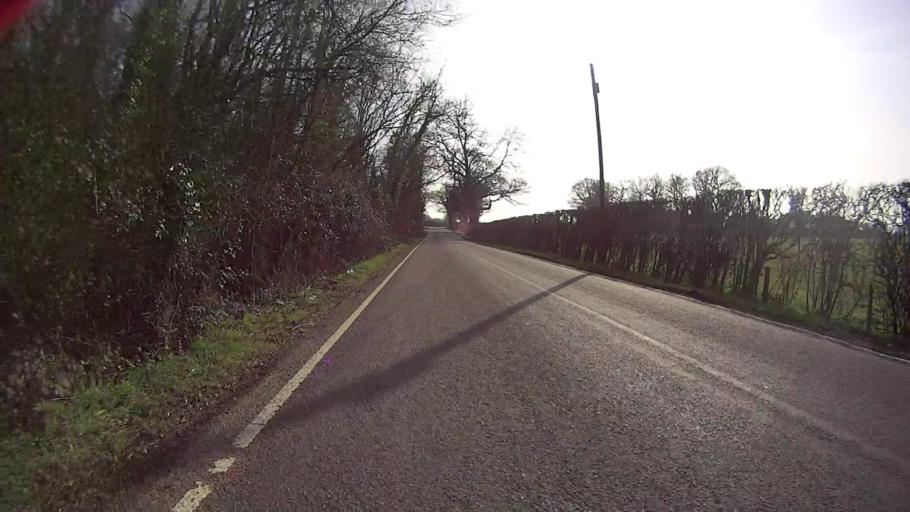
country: GB
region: England
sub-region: Surrey
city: Salfords
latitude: 51.2047
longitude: -0.1532
